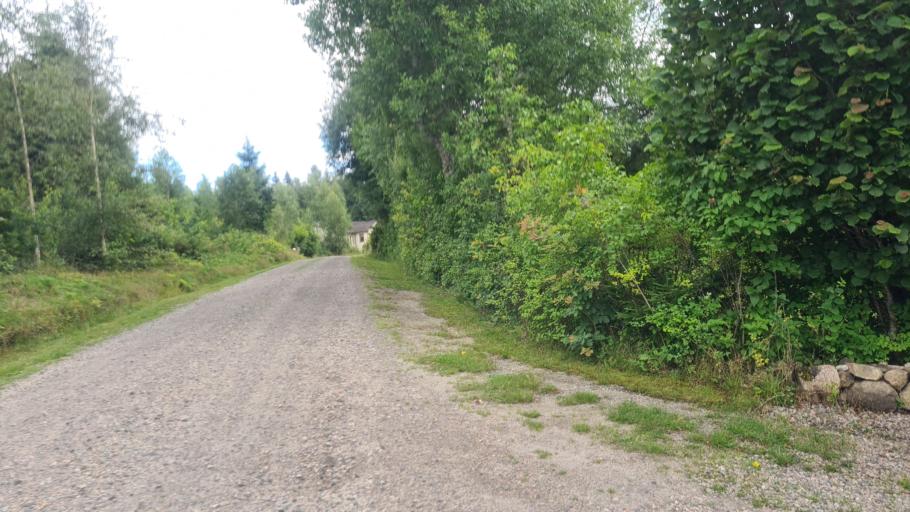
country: SE
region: Kronoberg
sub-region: Ljungby Kommun
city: Ljungby
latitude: 56.8216
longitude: 13.8632
